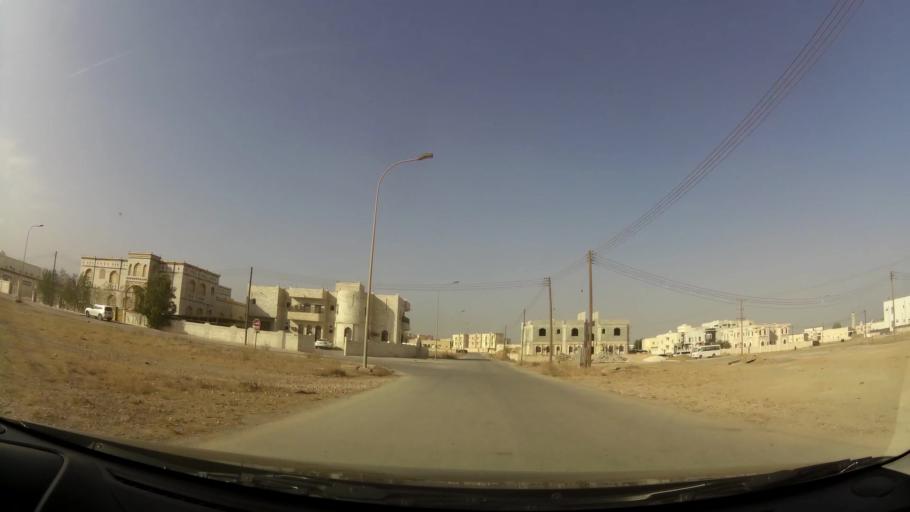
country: OM
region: Zufar
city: Salalah
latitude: 17.0215
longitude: 54.0200
